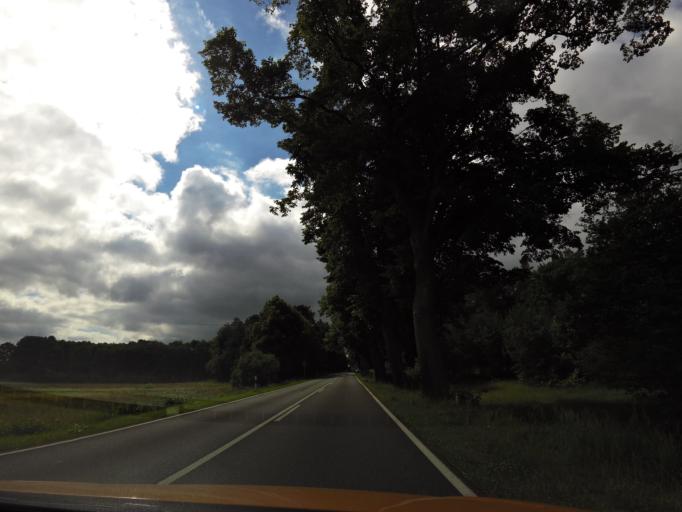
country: DE
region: Mecklenburg-Vorpommern
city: Muhl Rosin
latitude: 53.7576
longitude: 12.2478
